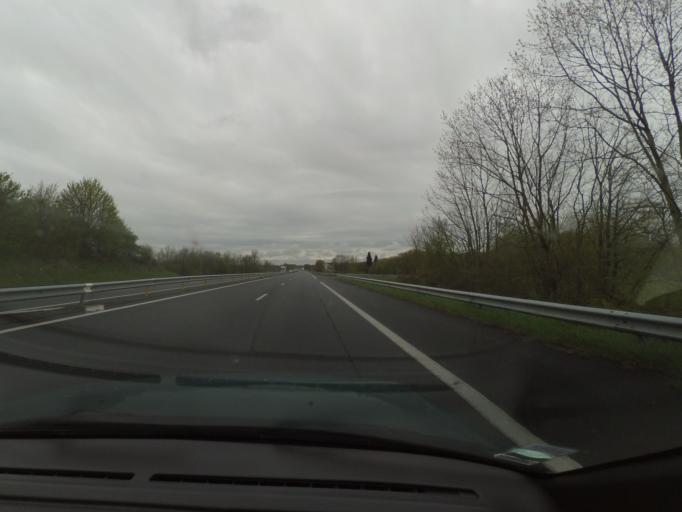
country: FR
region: Pays de la Loire
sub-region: Departement de la Sarthe
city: Vion
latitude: 47.7560
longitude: -0.2341
